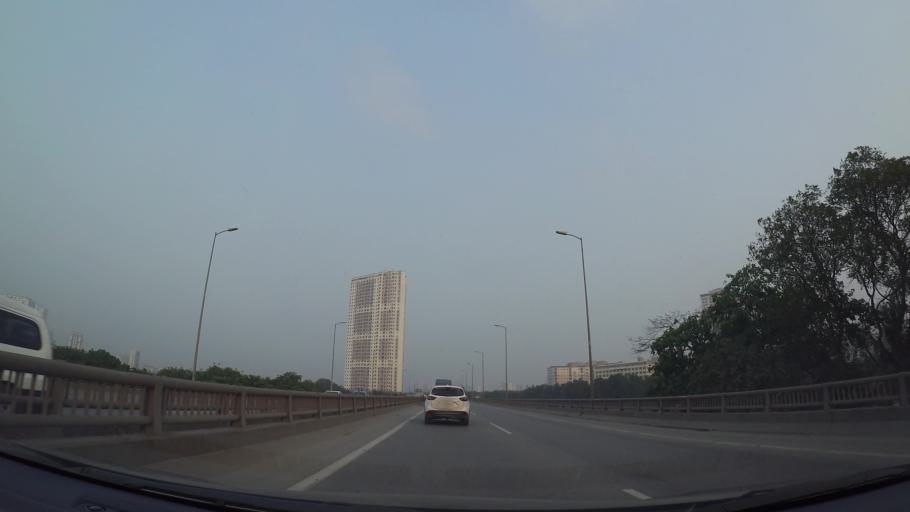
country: VN
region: Ha Noi
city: Van Dien
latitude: 20.9685
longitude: 105.8296
